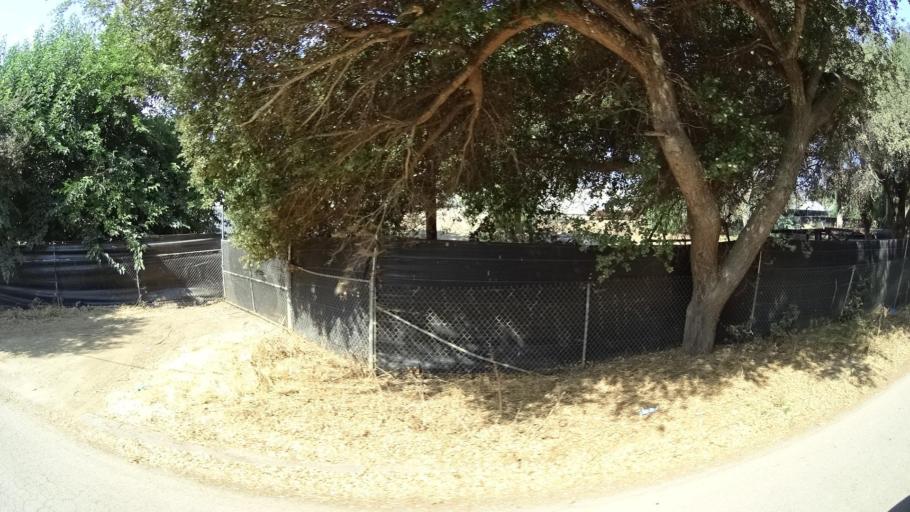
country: US
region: California
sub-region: San Diego County
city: San Marcos
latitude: 33.1946
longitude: -117.1608
